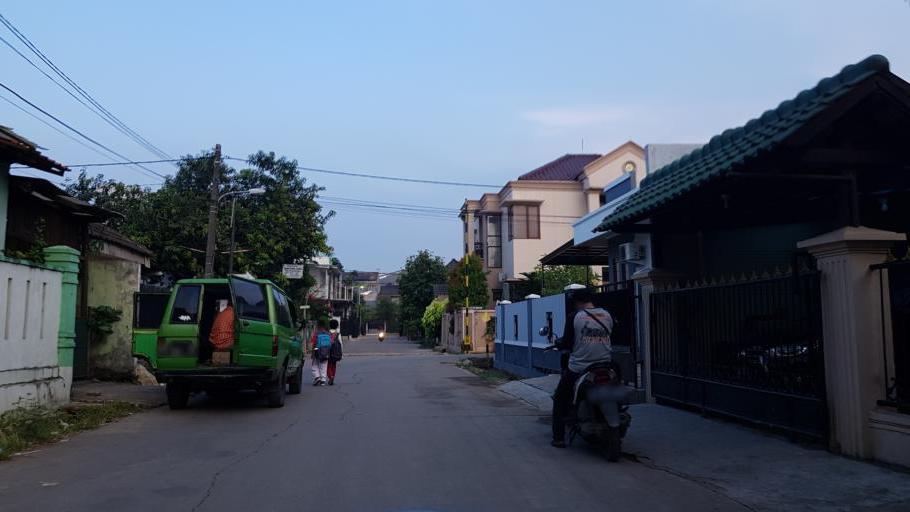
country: ID
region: West Java
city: Bekasi
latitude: -6.2663
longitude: 106.9479
